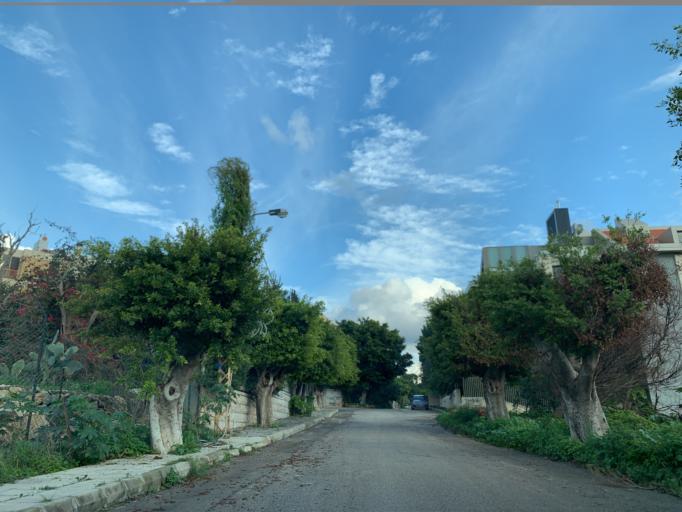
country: LB
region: Mont-Liban
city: Baabda
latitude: 33.8514
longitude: 35.5755
